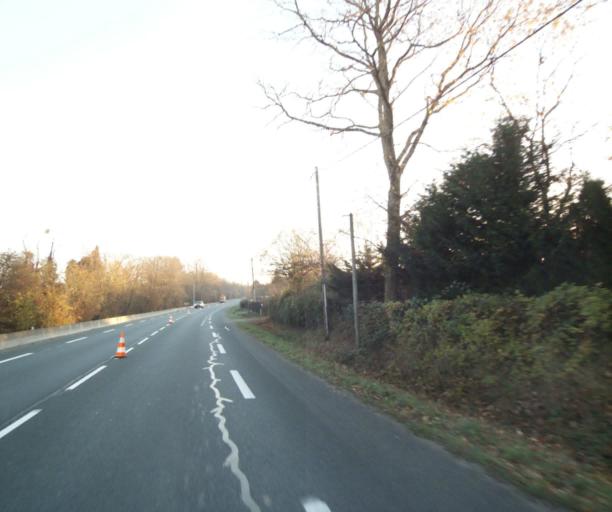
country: FR
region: Poitou-Charentes
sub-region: Departement de la Charente-Maritime
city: Fontcouverte
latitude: 45.7463
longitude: -0.5693
